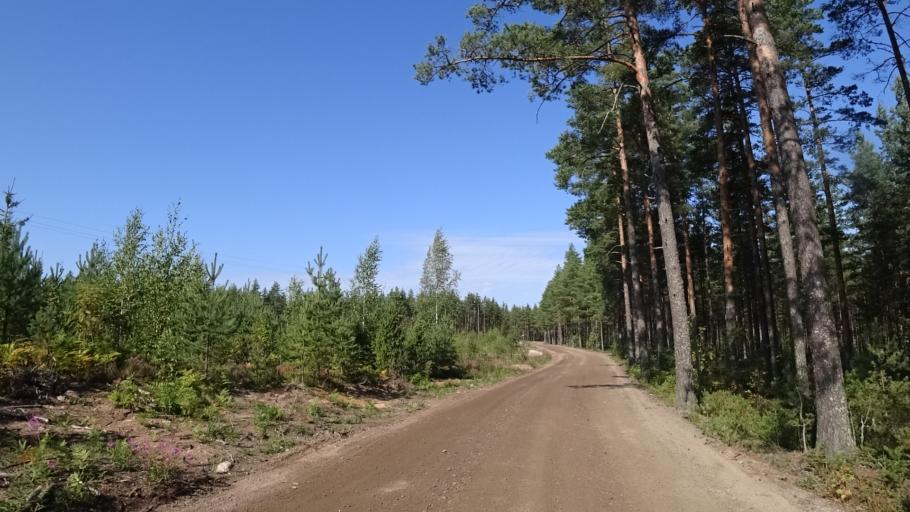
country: FI
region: Kymenlaakso
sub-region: Kotka-Hamina
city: Hamina
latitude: 60.5463
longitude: 27.2148
